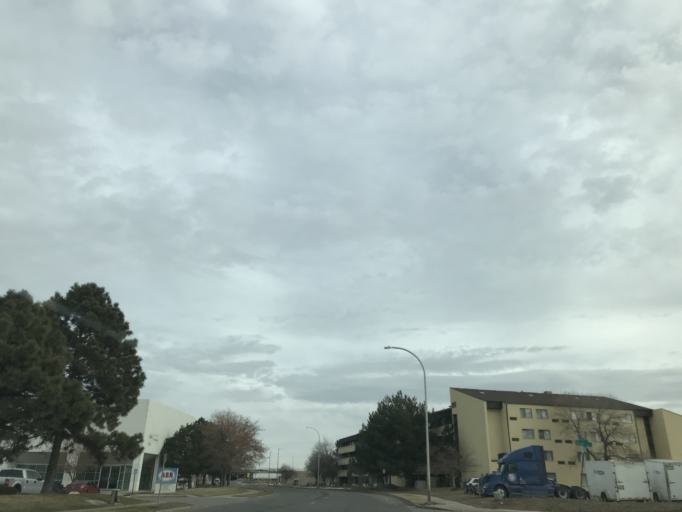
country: US
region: Colorado
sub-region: Adams County
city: Commerce City
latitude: 39.7824
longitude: -104.9062
